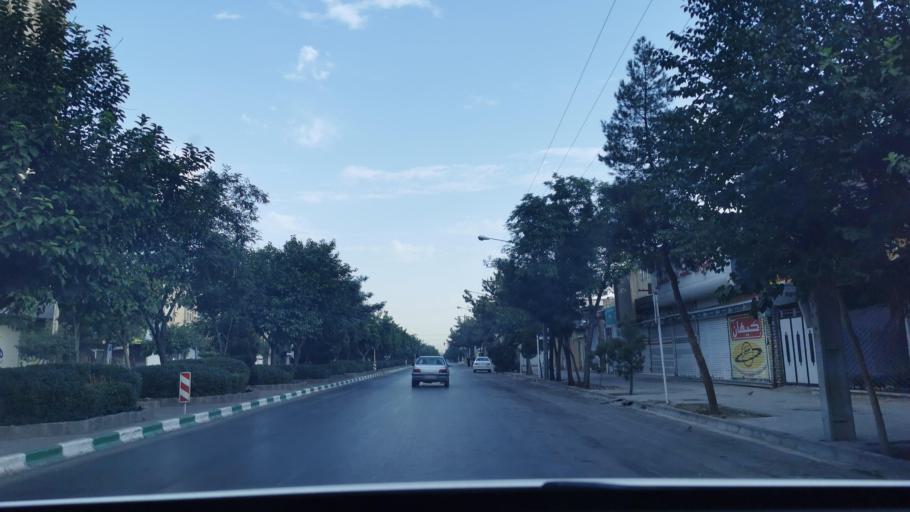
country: IR
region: Razavi Khorasan
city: Mashhad
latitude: 36.3592
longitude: 59.5239
